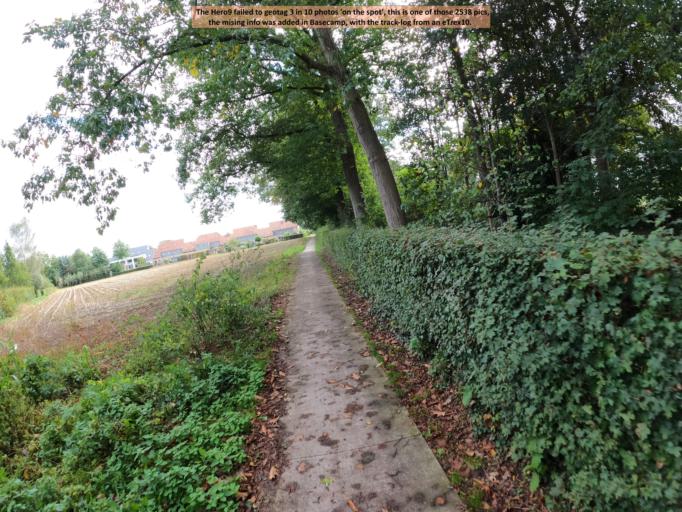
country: BE
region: Flanders
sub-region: Provincie Antwerpen
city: Boechout
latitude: 51.1611
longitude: 4.5053
